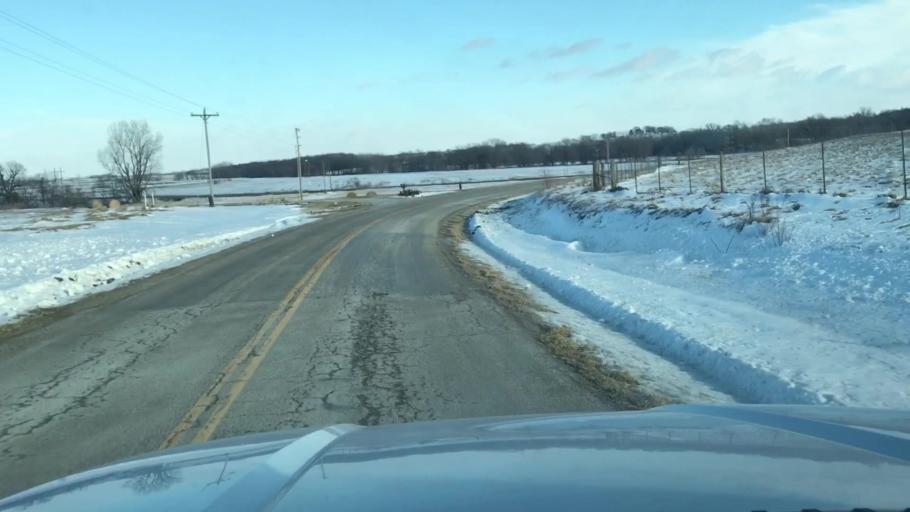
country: US
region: Missouri
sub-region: Holt County
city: Oregon
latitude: 40.1005
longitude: -94.9777
